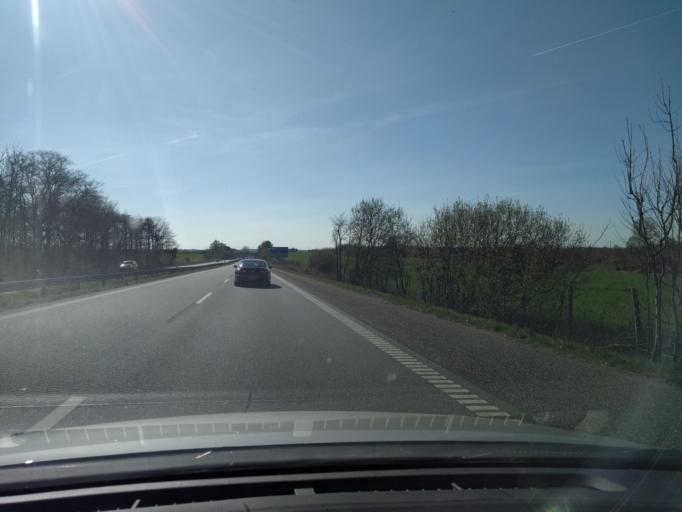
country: DK
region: South Denmark
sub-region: Nyborg Kommune
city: Nyborg
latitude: 55.3324
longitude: 10.7735
